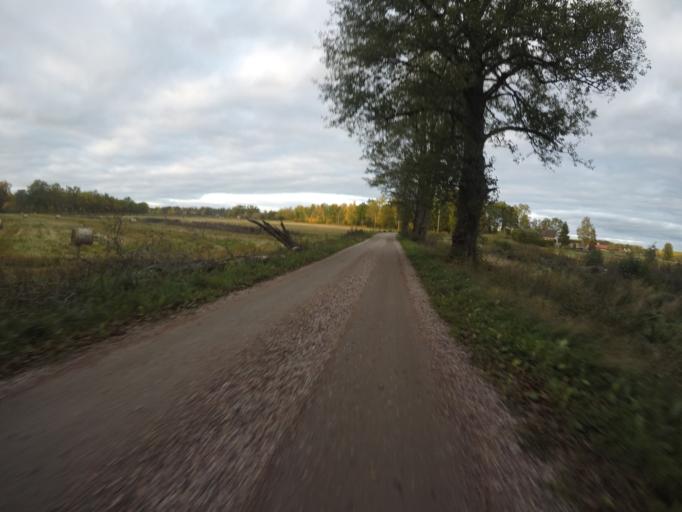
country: SE
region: Vaestmanland
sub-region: Arboga Kommun
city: Tyringe
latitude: 59.2956
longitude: 16.0047
